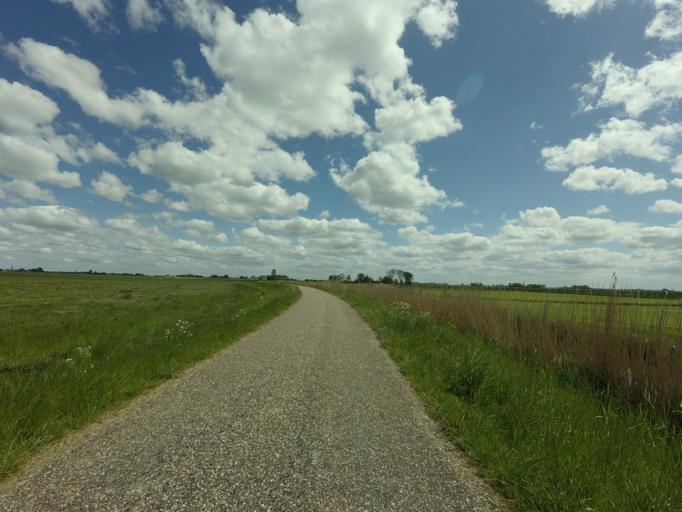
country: NL
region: Friesland
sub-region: Gemeente Franekeradeel
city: Franeker
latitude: 53.1459
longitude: 5.5002
